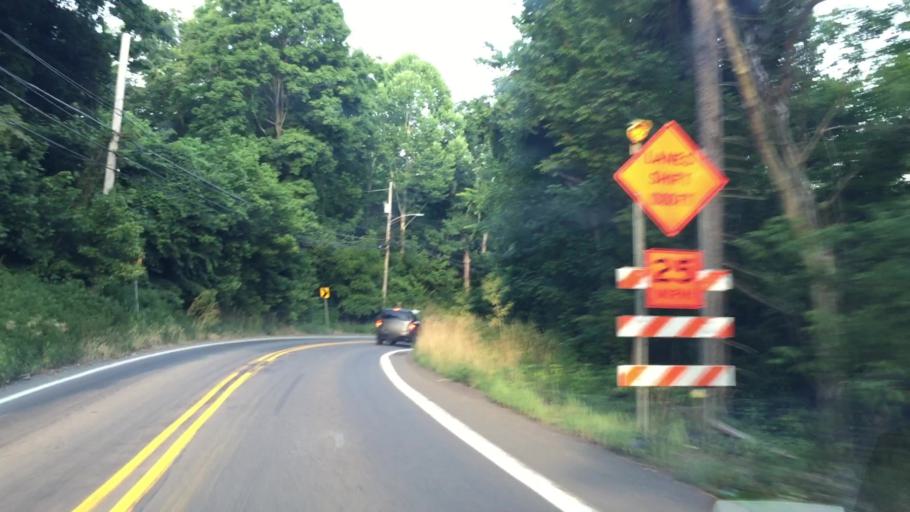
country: US
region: Pennsylvania
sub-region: Washington County
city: Thompsonville
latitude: 40.3196
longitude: -80.1191
